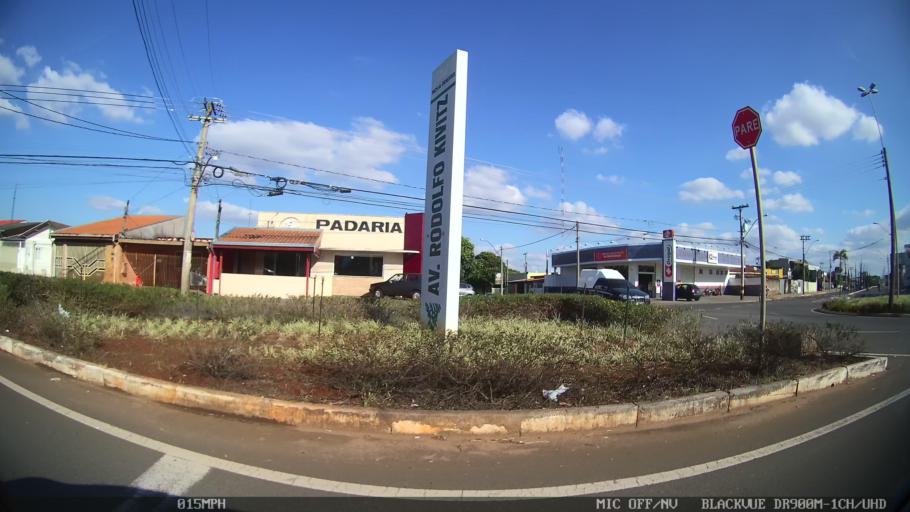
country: BR
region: Sao Paulo
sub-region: Nova Odessa
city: Nova Odessa
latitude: -22.7891
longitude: -47.3037
